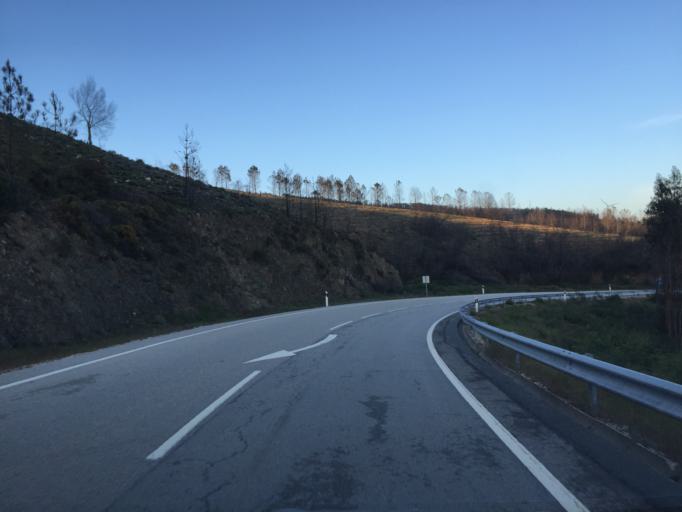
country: PT
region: Coimbra
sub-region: Pampilhosa da Serra
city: Pampilhosa da Serra
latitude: 40.1058
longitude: -8.0050
